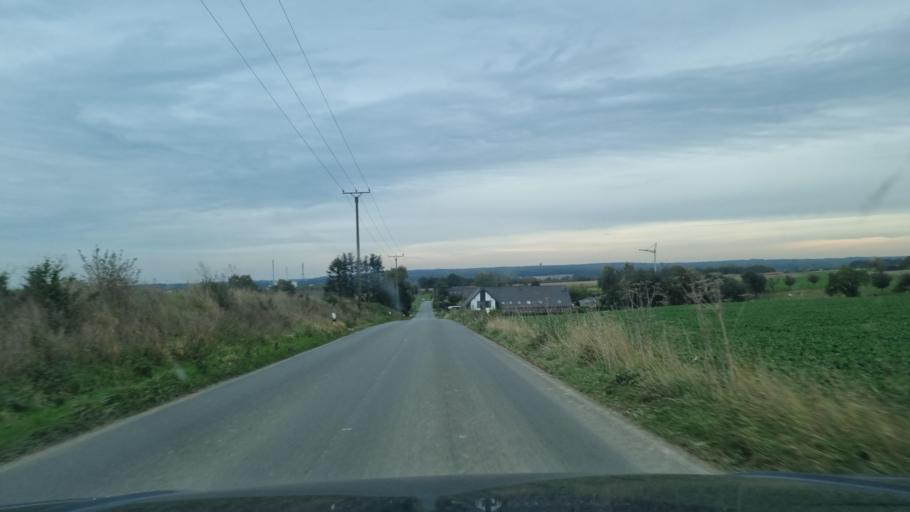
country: DE
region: North Rhine-Westphalia
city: Kalkar
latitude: 51.7054
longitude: 6.3079
